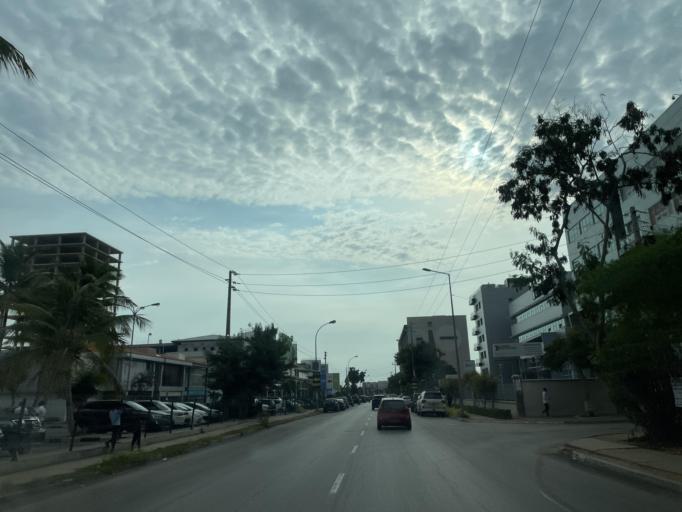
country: AO
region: Luanda
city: Luanda
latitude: -8.9177
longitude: 13.1881
